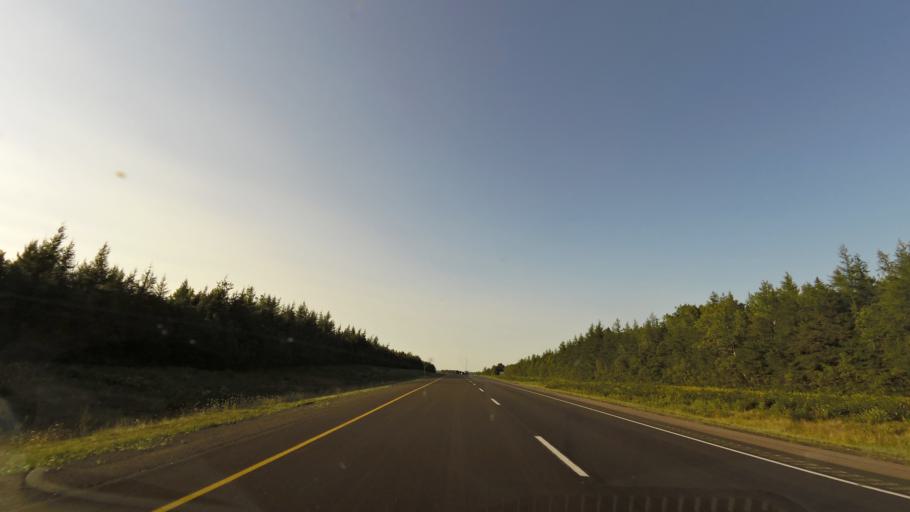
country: CA
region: New Brunswick
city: Dieppe
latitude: 46.0608
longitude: -64.5876
